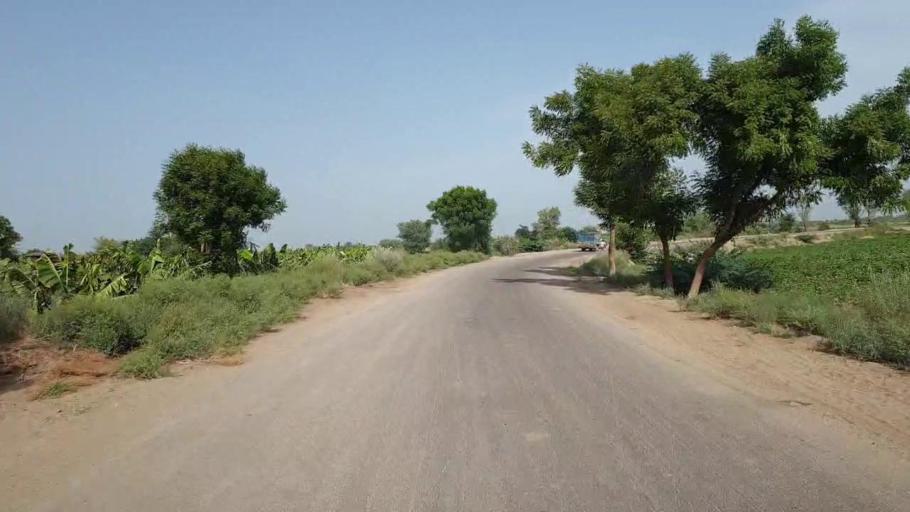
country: PK
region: Sindh
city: Sakrand
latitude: 26.2619
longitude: 68.2837
